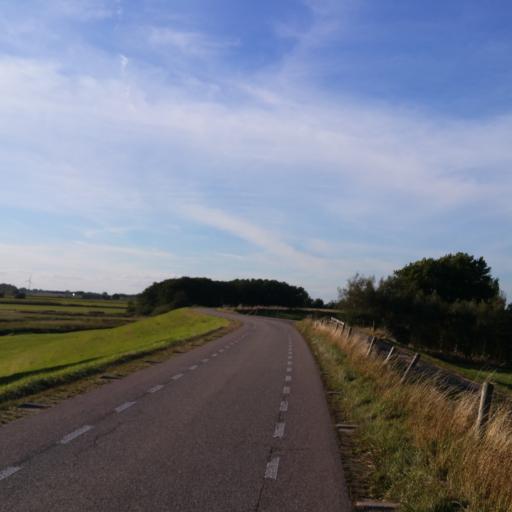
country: NL
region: Utrecht
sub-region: Gemeente IJsselstein
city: IJsselstein
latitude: 51.9746
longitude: 5.0243
